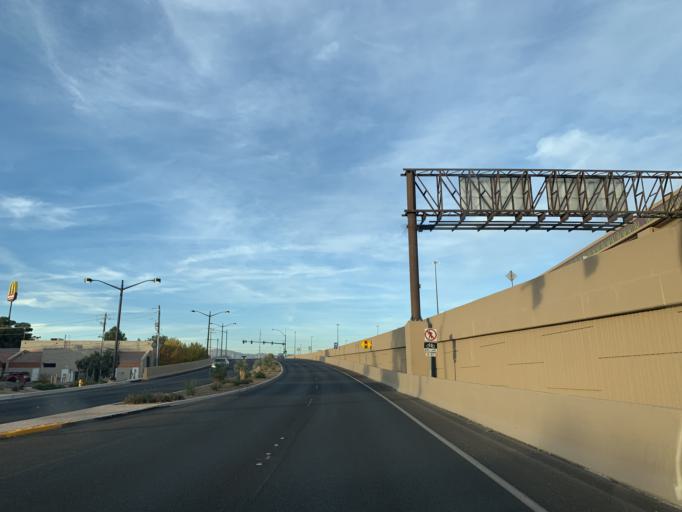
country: US
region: Nevada
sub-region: Clark County
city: Las Vegas
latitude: 36.1549
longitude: -115.1628
